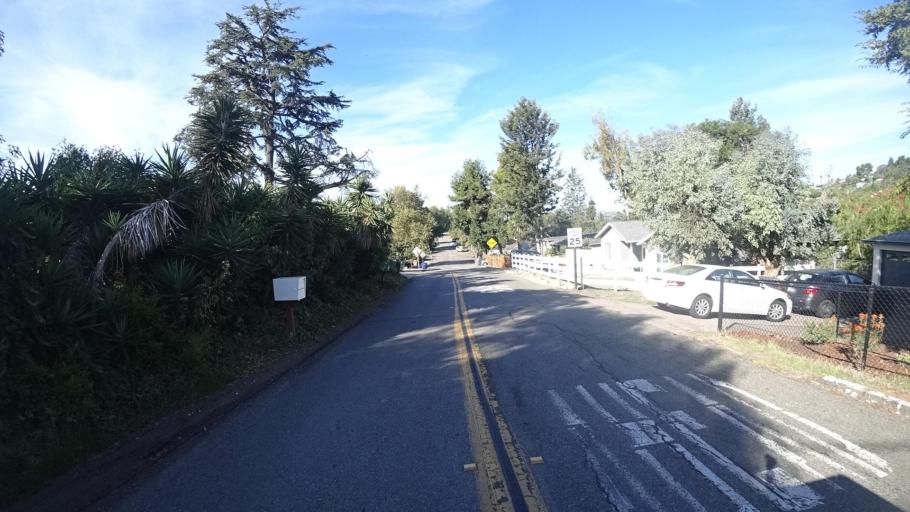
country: US
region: California
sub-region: San Diego County
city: Casa de Oro-Mount Helix
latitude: 32.7423
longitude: -116.9652
